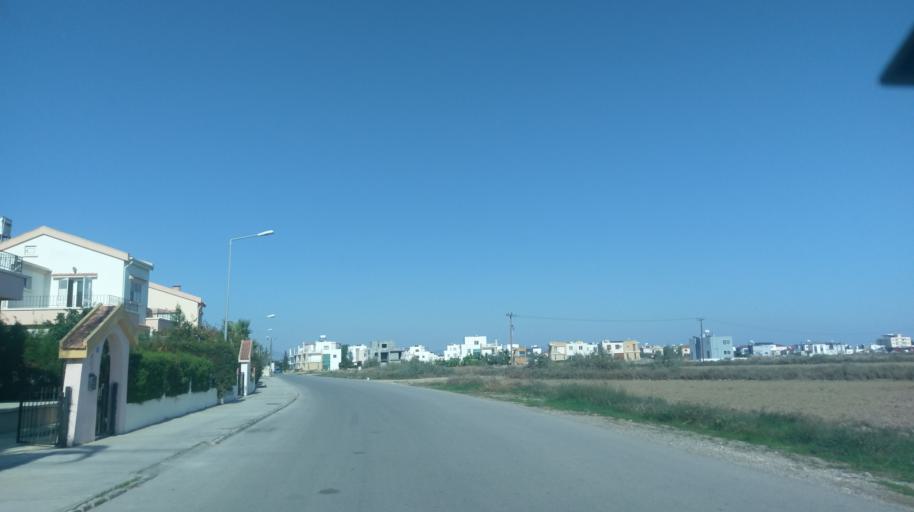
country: CY
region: Ammochostos
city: Acheritou
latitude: 35.1526
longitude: 33.8848
